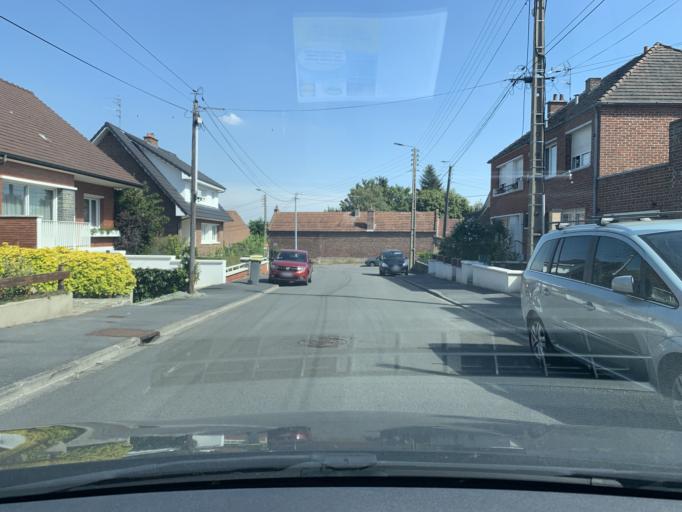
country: FR
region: Nord-Pas-de-Calais
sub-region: Departement du Nord
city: Cambrai
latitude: 50.1651
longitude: 3.2343
